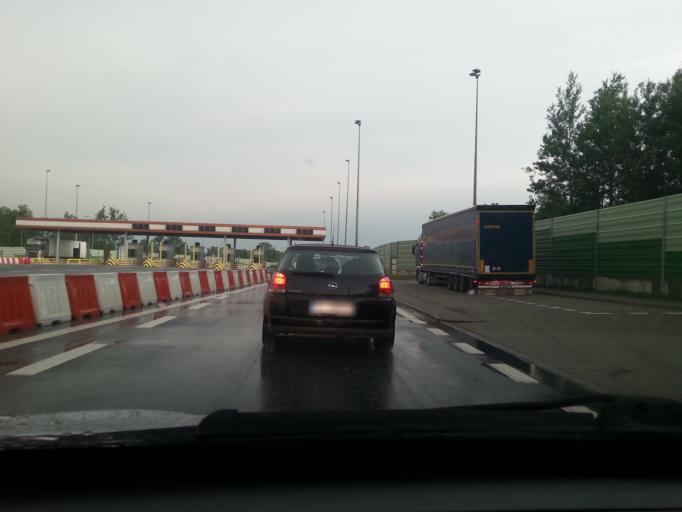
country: PL
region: Lodz Voivodeship
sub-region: Powiat zgierski
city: Strykow
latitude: 51.8858
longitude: 19.5846
